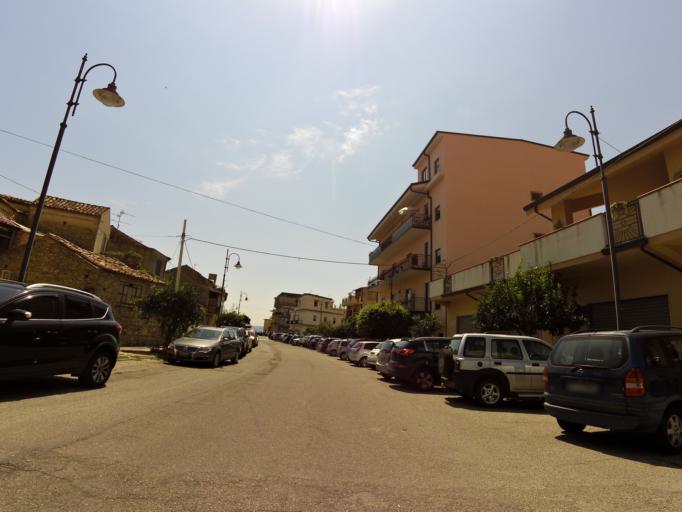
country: IT
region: Calabria
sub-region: Provincia di Reggio Calabria
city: Roccella Ionica
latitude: 38.3245
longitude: 16.4099
